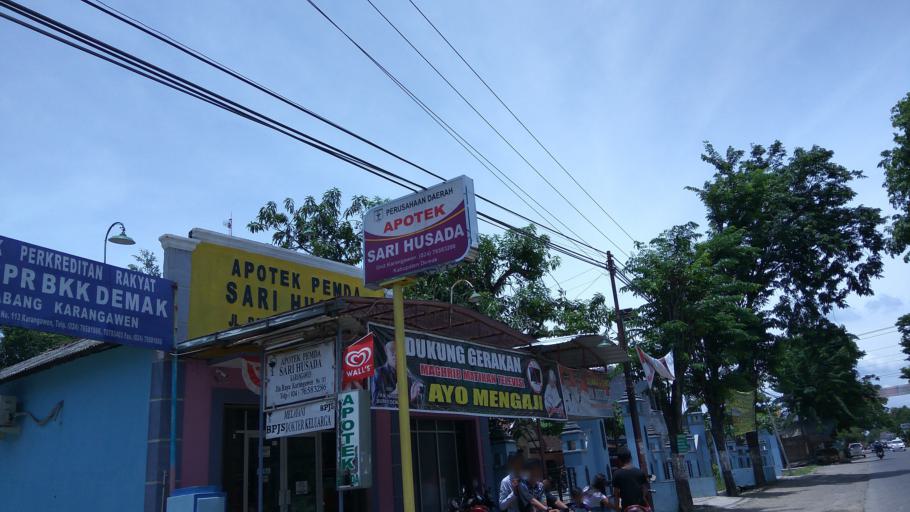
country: ID
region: Central Java
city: Mranggen
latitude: -7.0442
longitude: 110.5750
